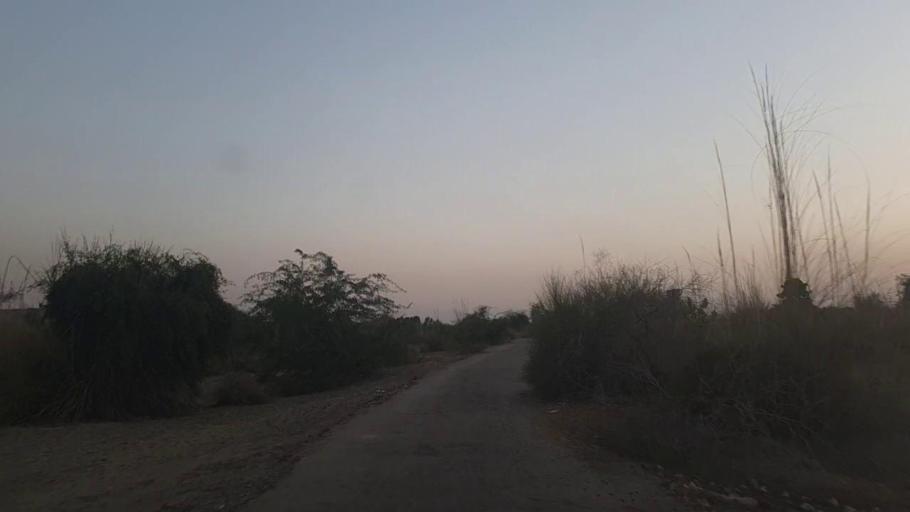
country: PK
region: Sindh
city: Jam Sahib
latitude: 26.3896
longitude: 68.8094
